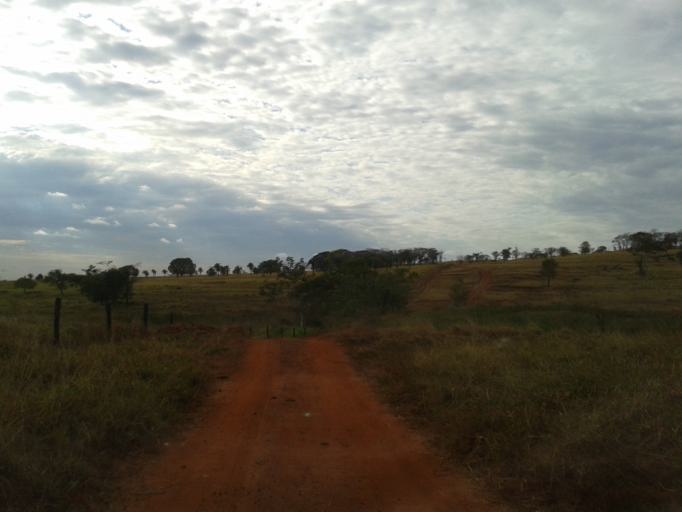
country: BR
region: Minas Gerais
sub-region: Santa Vitoria
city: Santa Vitoria
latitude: -18.7336
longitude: -50.2369
